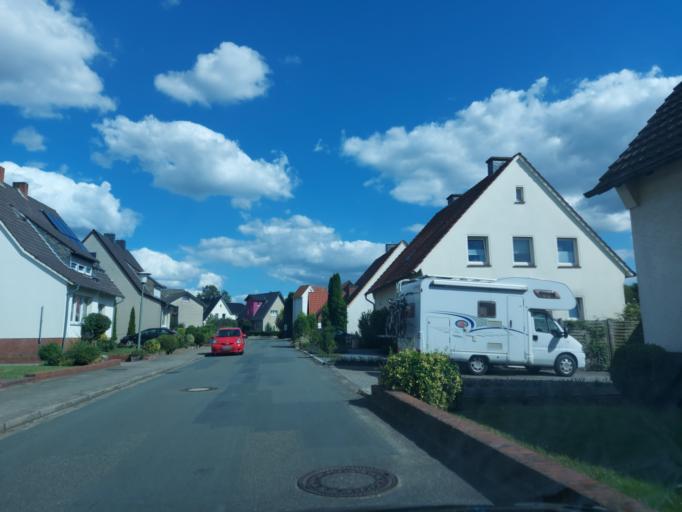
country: DE
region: Lower Saxony
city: Hagen
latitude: 52.1952
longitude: 7.9746
